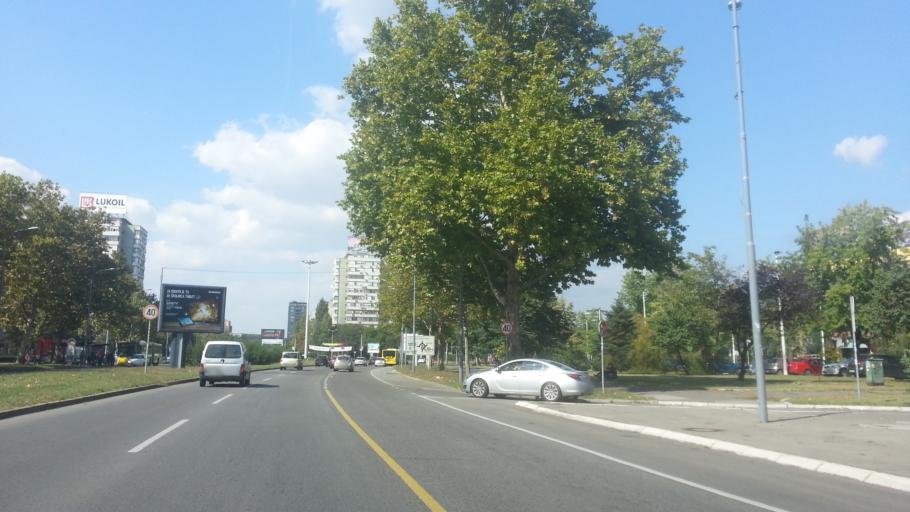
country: RS
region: Central Serbia
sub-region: Belgrade
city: Novi Beograd
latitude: 44.8233
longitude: 20.4155
